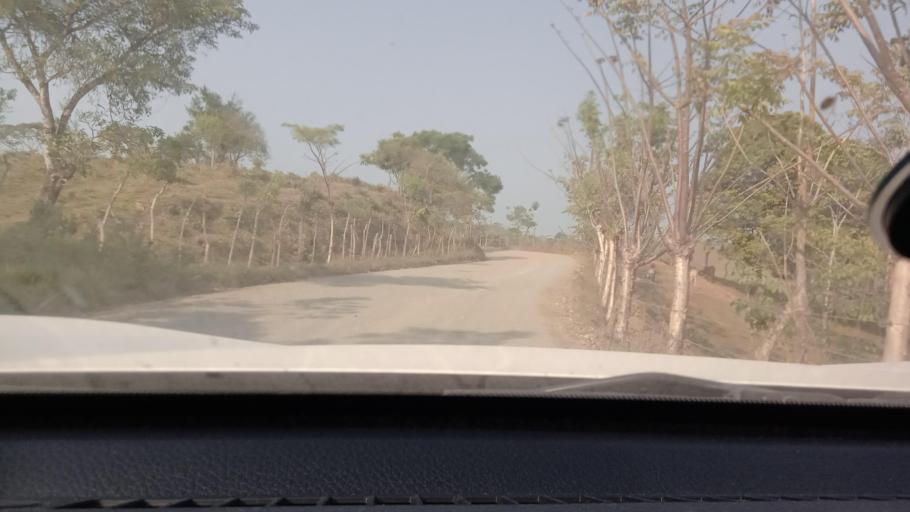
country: MX
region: Tabasco
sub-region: Huimanguillo
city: Francisco Rueda
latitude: 17.6519
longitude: -93.8994
